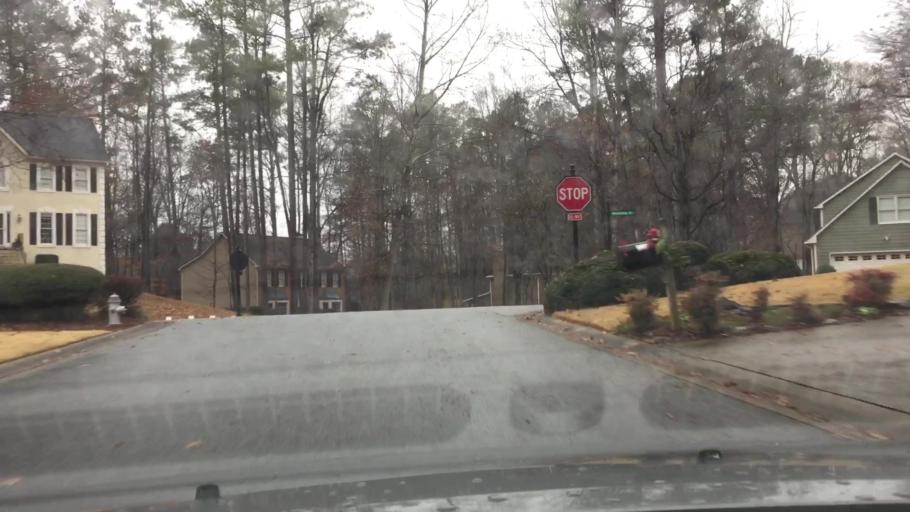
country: US
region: Georgia
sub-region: Cobb County
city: Fair Oaks
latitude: 33.9131
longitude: -84.6148
